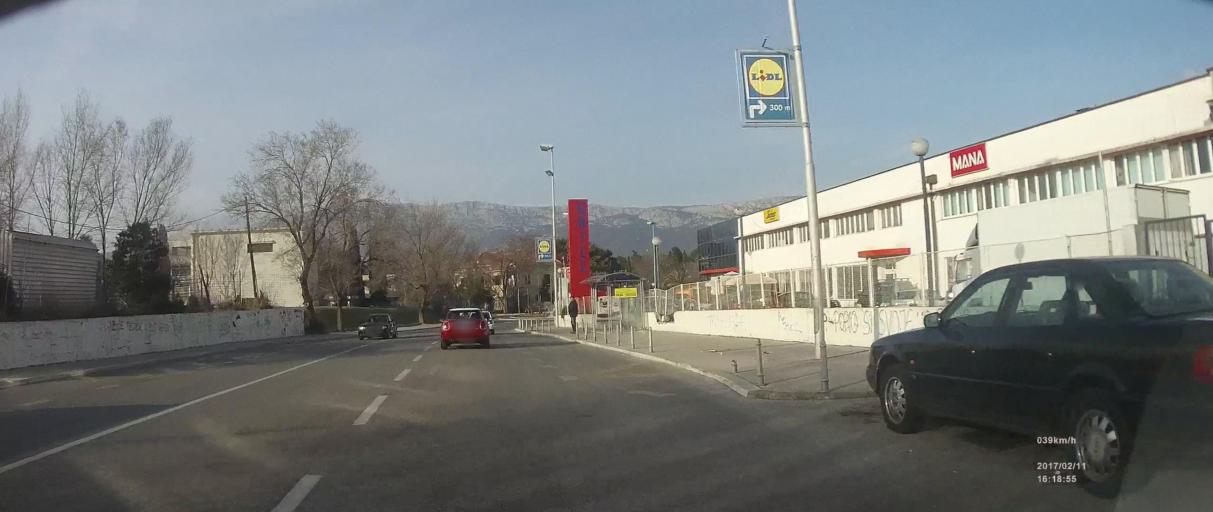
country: HR
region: Splitsko-Dalmatinska
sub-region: Grad Split
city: Split
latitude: 43.5227
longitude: 16.4332
